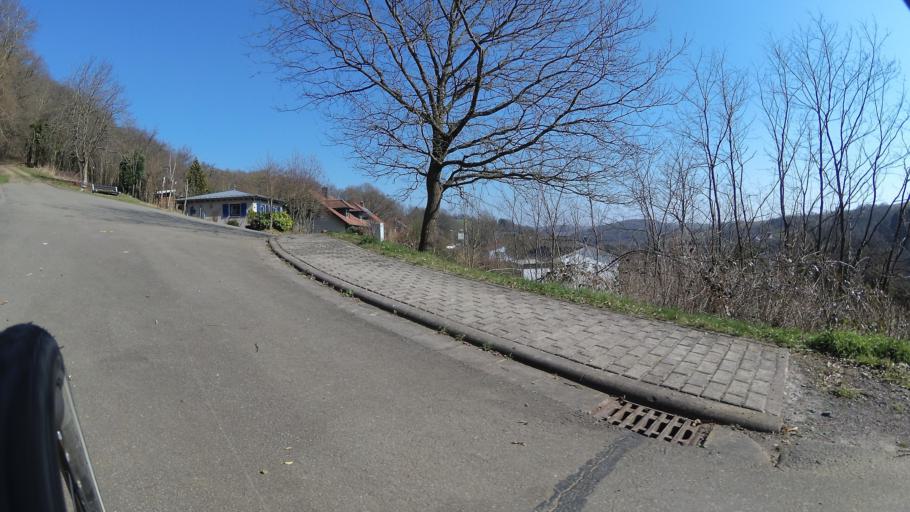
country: DE
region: Rheinland-Pfalz
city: Ruthweiler
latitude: 49.5558
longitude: 7.3640
